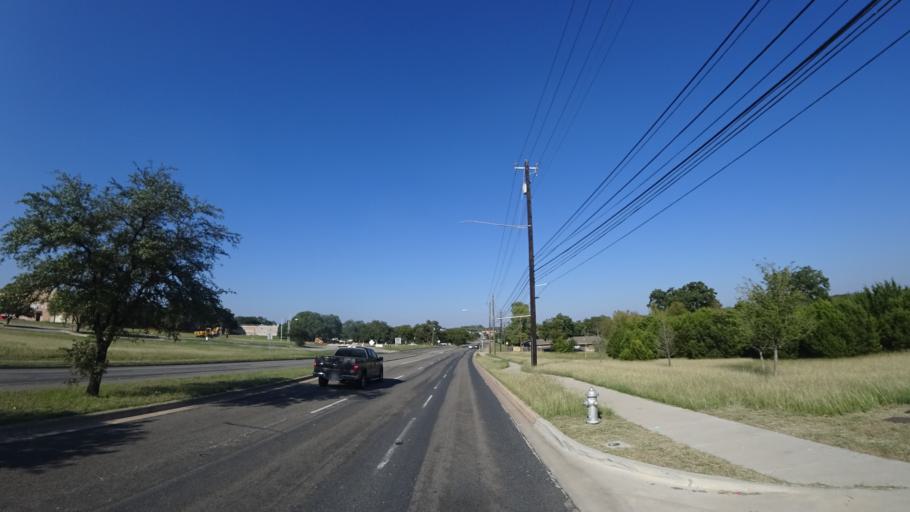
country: US
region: Texas
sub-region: Travis County
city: Austin
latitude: 30.3404
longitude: -97.6811
